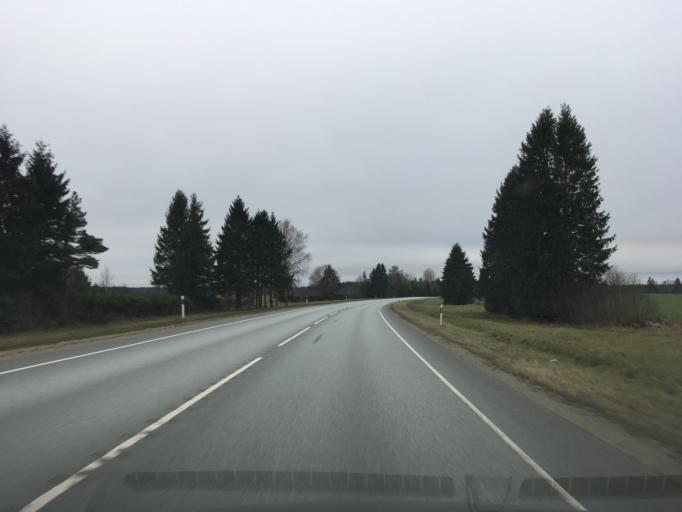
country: EE
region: Laeaene-Virumaa
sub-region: Viru-Nigula vald
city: Kunda
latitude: 59.3868
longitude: 26.6147
